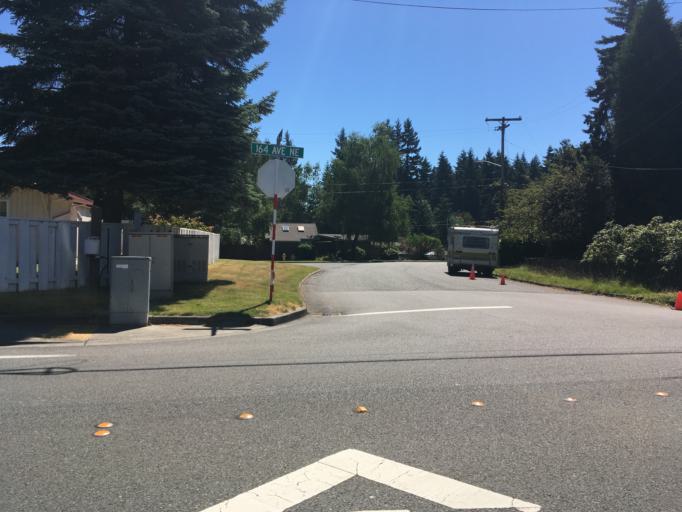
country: US
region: Washington
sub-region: King County
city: Sammamish
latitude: 47.6252
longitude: -122.1217
